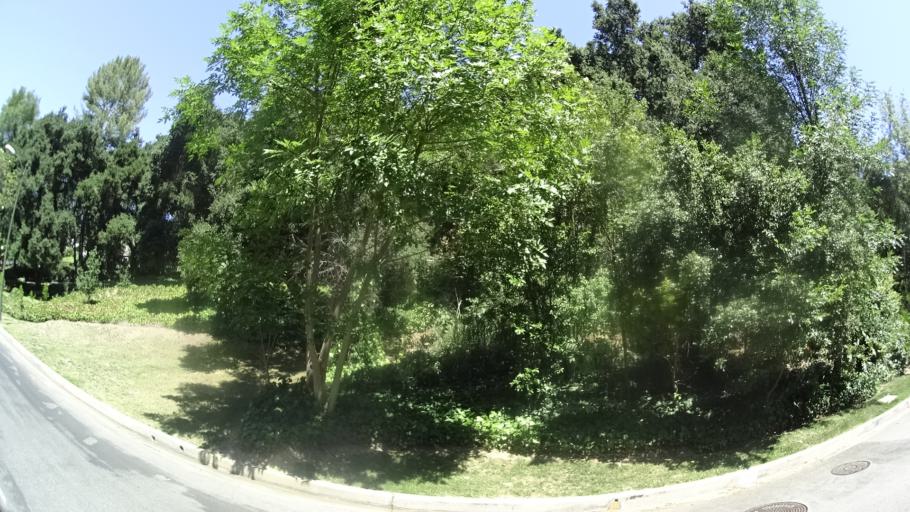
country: US
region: California
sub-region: Los Angeles County
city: Sherman Oaks
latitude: 34.1475
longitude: -118.4821
